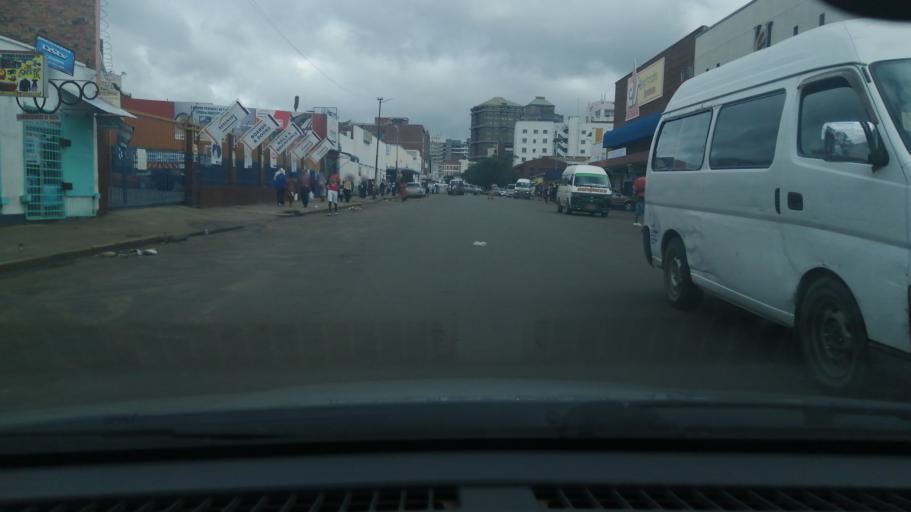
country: ZW
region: Harare
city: Harare
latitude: -17.8348
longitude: 31.0442
